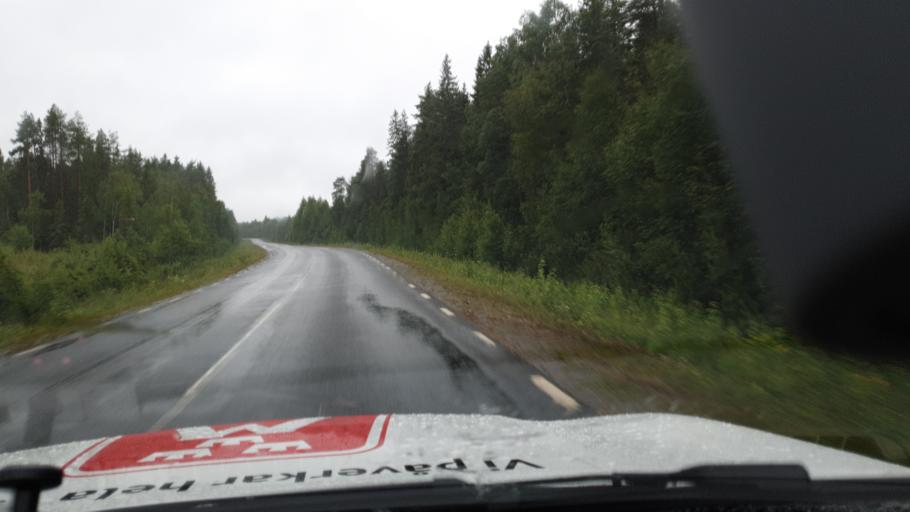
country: SE
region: Vaesterbotten
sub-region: Skelleftea Kommun
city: Soedra Bergsbyn
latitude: 64.5881
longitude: 21.0346
